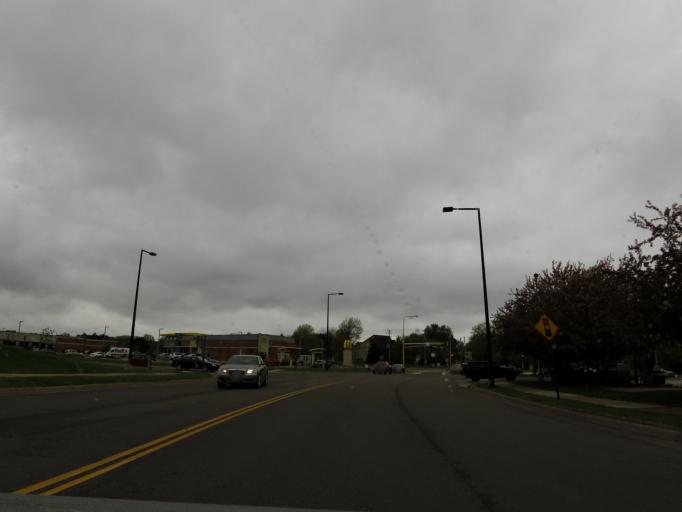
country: US
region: Minnesota
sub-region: Washington County
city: Stillwater
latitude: 45.0431
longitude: -92.8380
